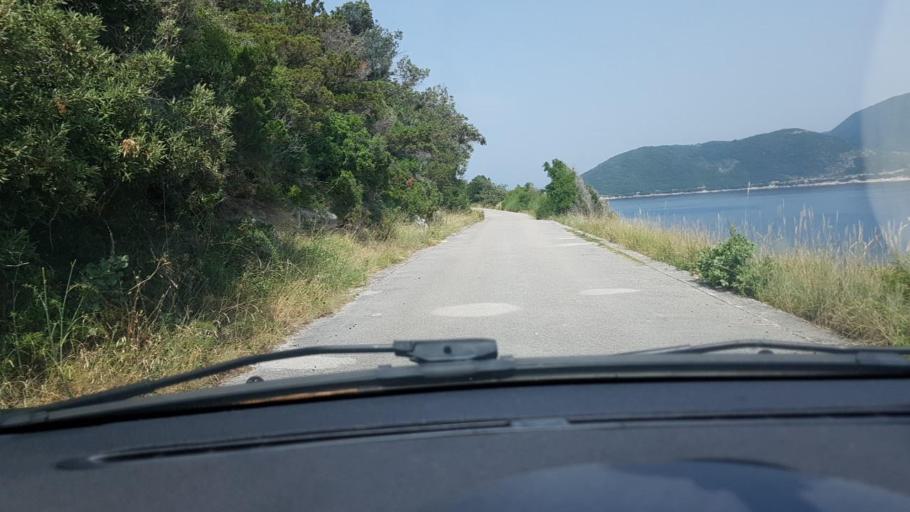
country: ME
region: Herceg Novi
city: Herceg-Novi
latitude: 42.3954
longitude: 18.5287
